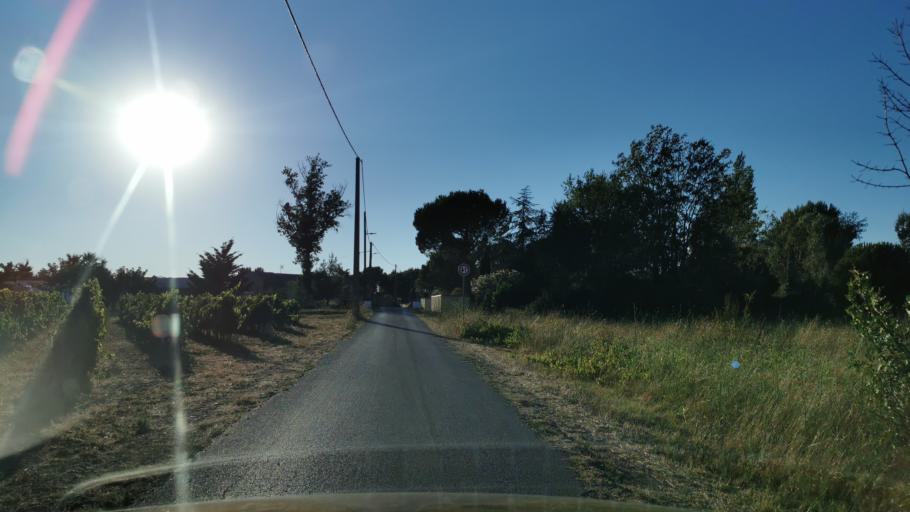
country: FR
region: Languedoc-Roussillon
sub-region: Departement de l'Aude
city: Coursan
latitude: 43.2663
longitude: 3.0188
